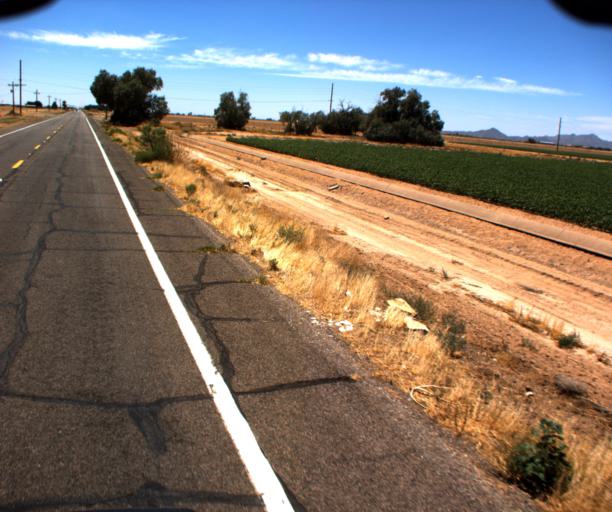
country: US
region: Arizona
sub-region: Pinal County
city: Coolidge
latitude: 32.8795
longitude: -111.5302
